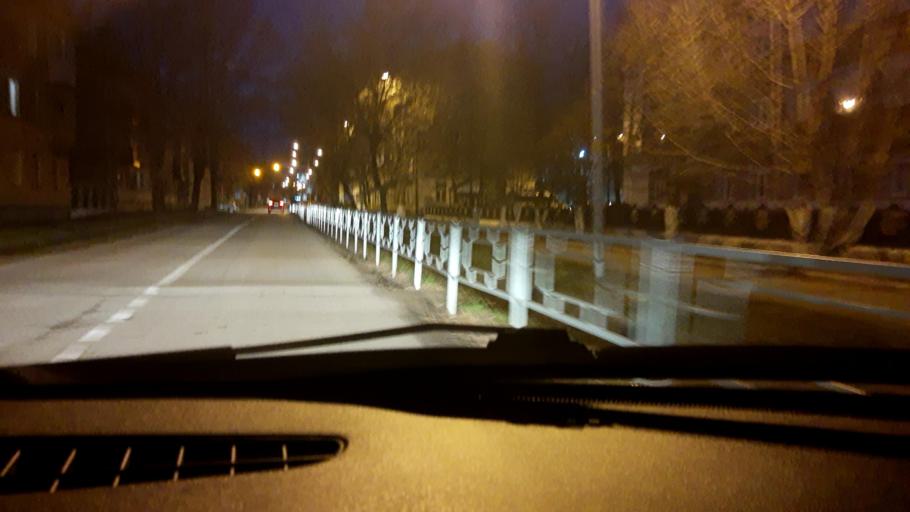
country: RU
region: Bashkortostan
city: Mikhaylovka
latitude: 54.7064
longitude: 55.8390
